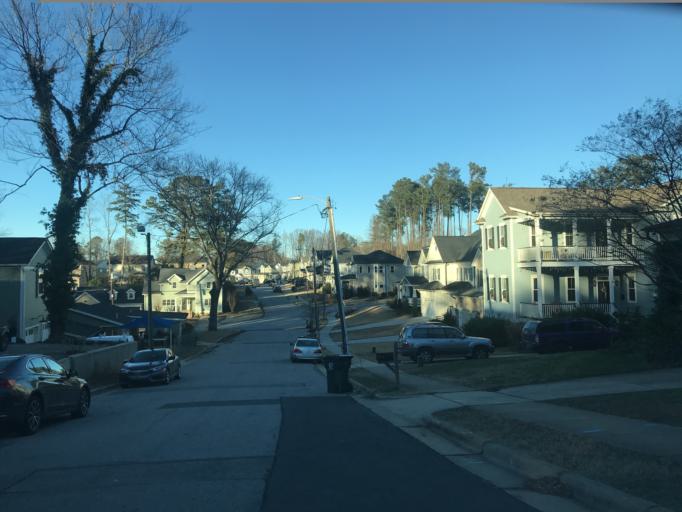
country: US
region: North Carolina
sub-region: Wake County
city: Raleigh
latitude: 35.7930
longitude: -78.6203
